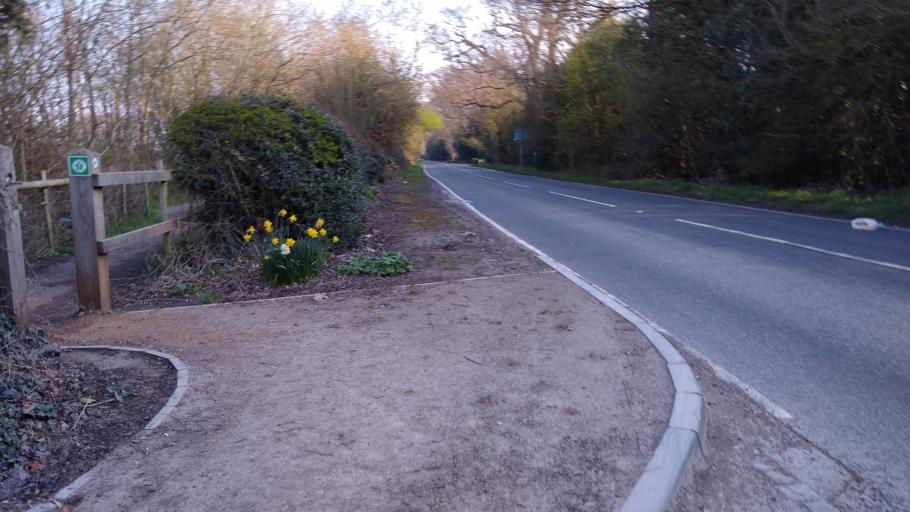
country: GB
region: England
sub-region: Wokingham
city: Woodley
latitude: 51.4511
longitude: -0.8630
